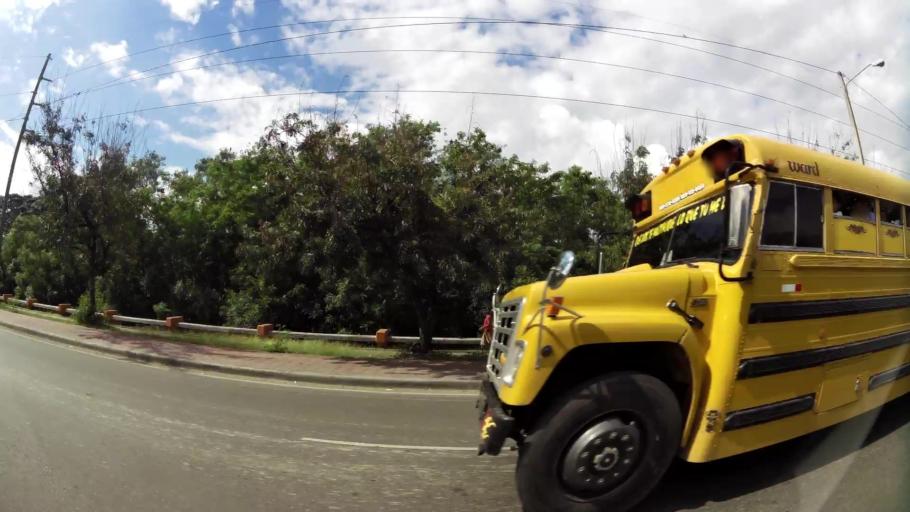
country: DO
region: Santiago
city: Santiago de los Caballeros
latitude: 19.4687
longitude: -70.7150
